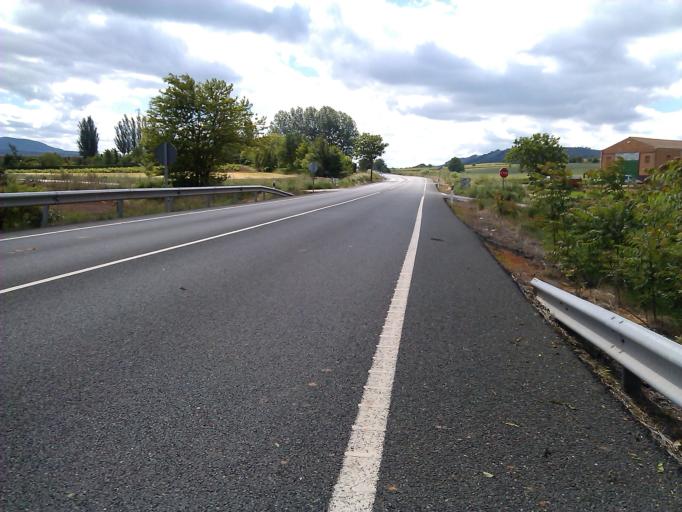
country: ES
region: La Rioja
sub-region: Provincia de La Rioja
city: Hormilla
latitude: 42.4328
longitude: -2.7830
